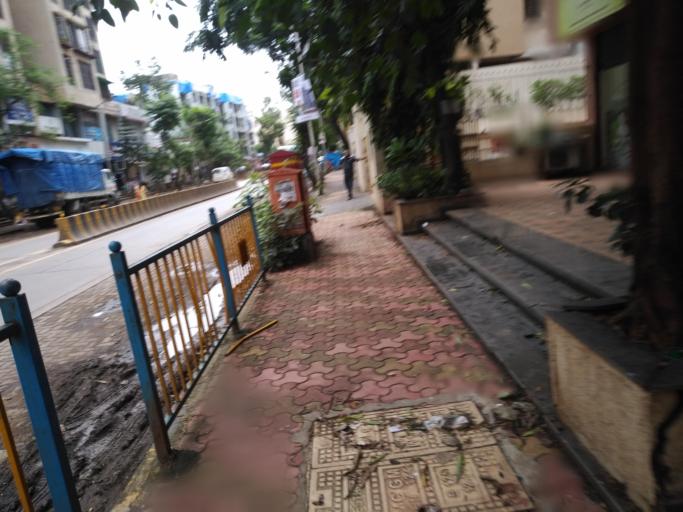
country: IN
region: Maharashtra
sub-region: Mumbai Suburban
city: Borivli
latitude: 19.2358
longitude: 72.8640
